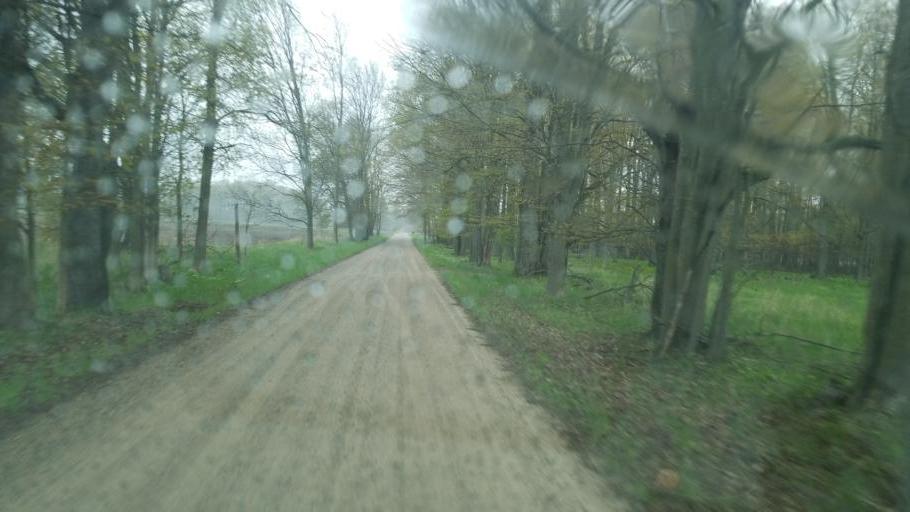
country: US
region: Michigan
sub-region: Mecosta County
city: Canadian Lakes
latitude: 43.5168
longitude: -85.3139
